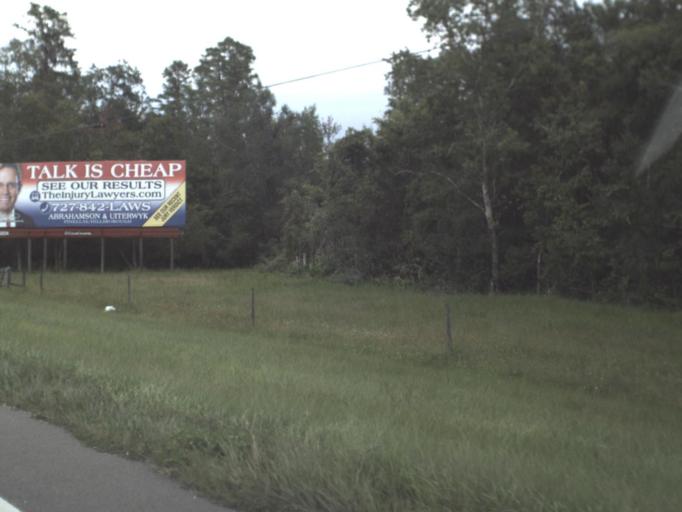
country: US
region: Florida
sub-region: Pasco County
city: Shady Hills
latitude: 28.3324
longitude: -82.5014
